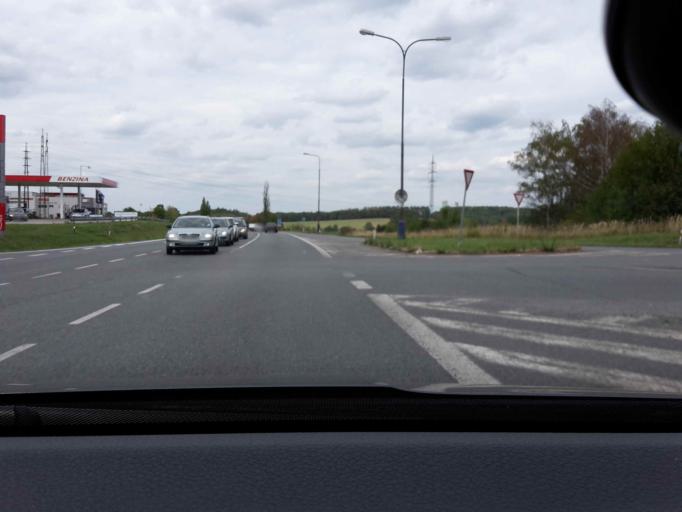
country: CZ
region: Central Bohemia
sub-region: Okres Benesov
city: Benesov
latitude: 49.7938
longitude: 14.6795
